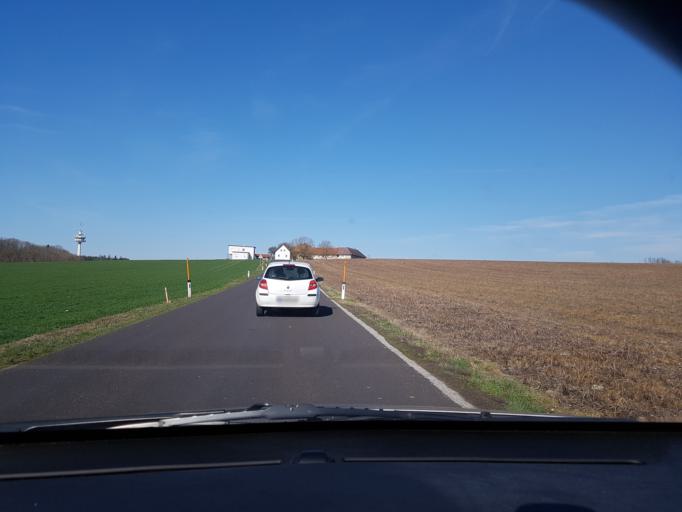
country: AT
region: Upper Austria
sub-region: Politischer Bezirk Linz-Land
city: Ansfelden
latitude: 48.2020
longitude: 14.3124
